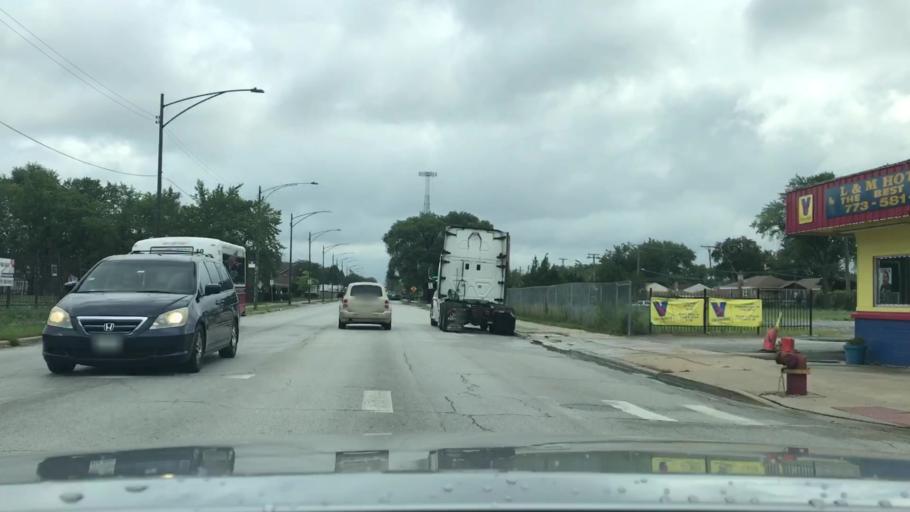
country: US
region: Illinois
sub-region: Cook County
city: Stickney
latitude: 41.8075
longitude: -87.7517
